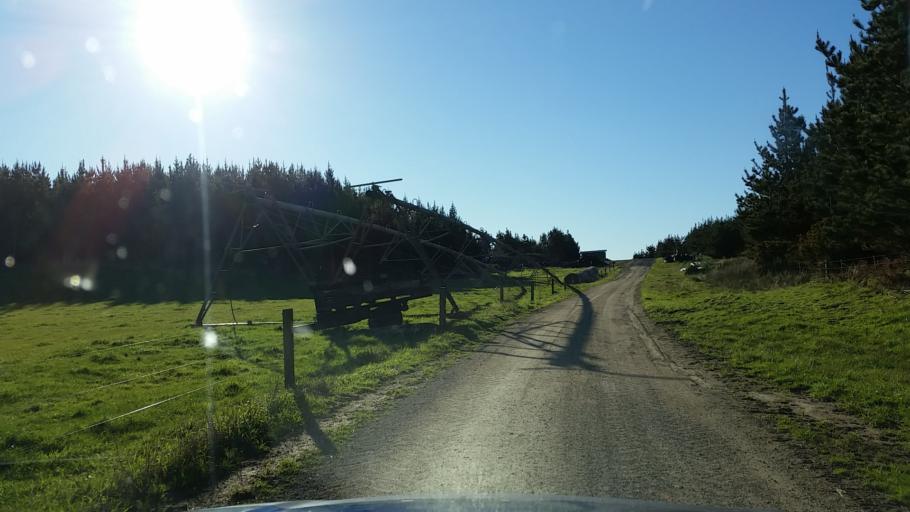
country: NZ
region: Taranaki
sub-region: South Taranaki District
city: Patea
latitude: -39.8336
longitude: 174.6819
